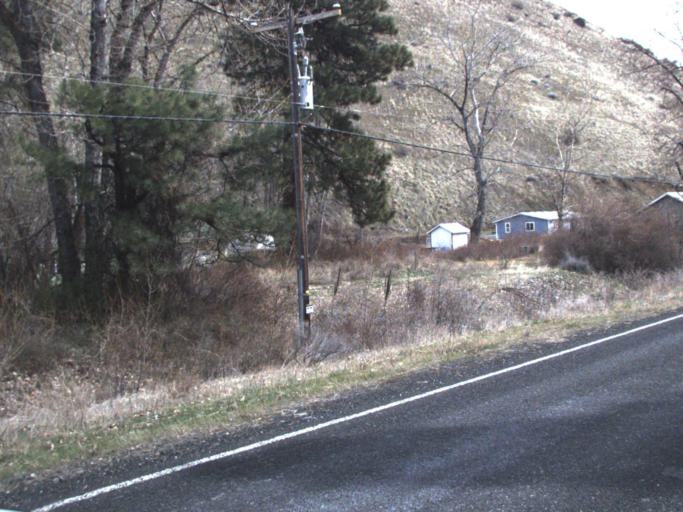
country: US
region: Washington
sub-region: Yakima County
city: Tieton
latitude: 46.7748
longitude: -120.8550
